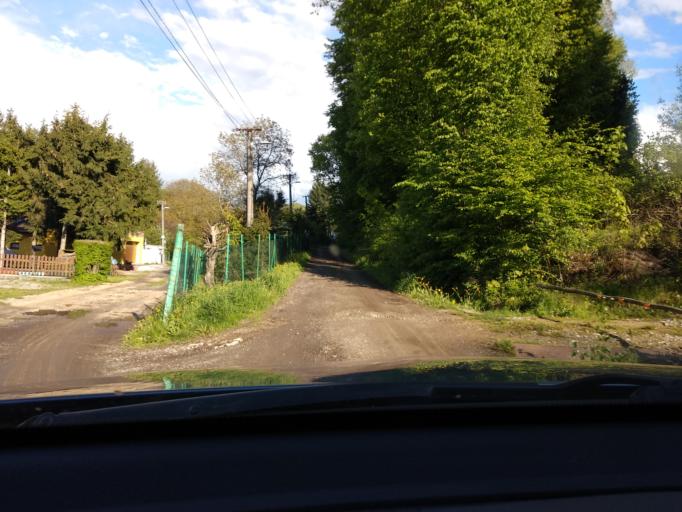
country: SK
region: Trenciansky
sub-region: Okres Trencin
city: Trencin
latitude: 48.8157
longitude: 18.0811
